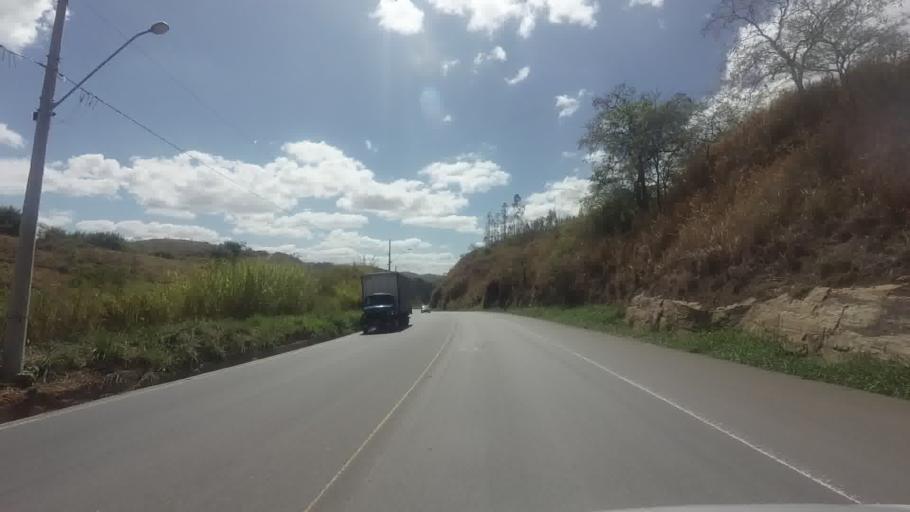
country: BR
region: Minas Gerais
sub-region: Alem Paraiba
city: Alem Paraiba
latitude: -21.8621
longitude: -42.6686
